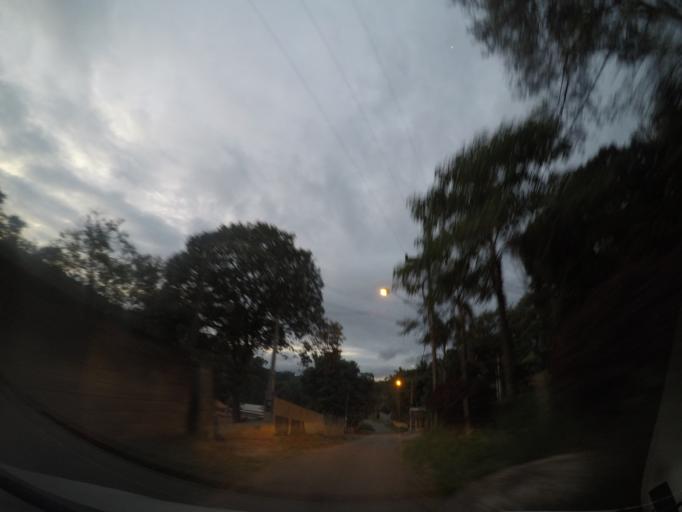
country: BR
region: Sao Paulo
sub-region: Aruja
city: Aruja
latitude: -23.3491
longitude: -46.2878
